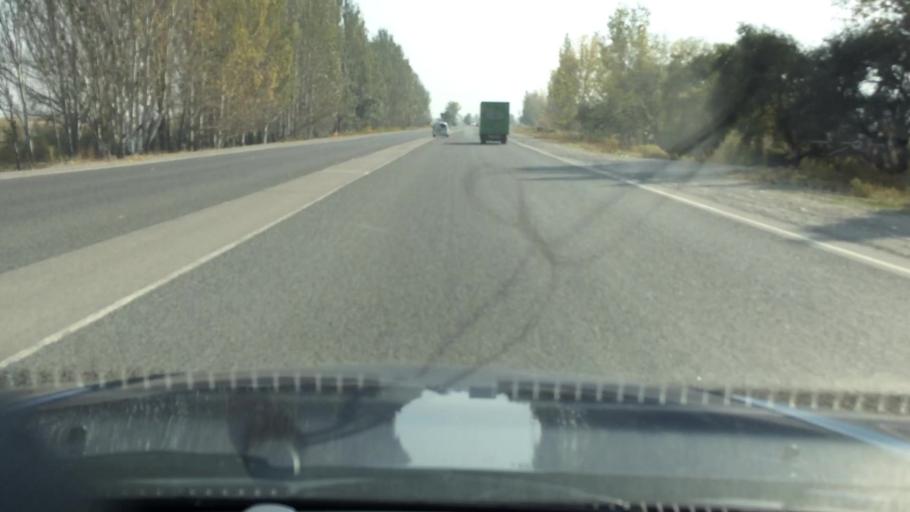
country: KG
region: Chuy
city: Ivanovka
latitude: 42.9359
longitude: 74.9911
